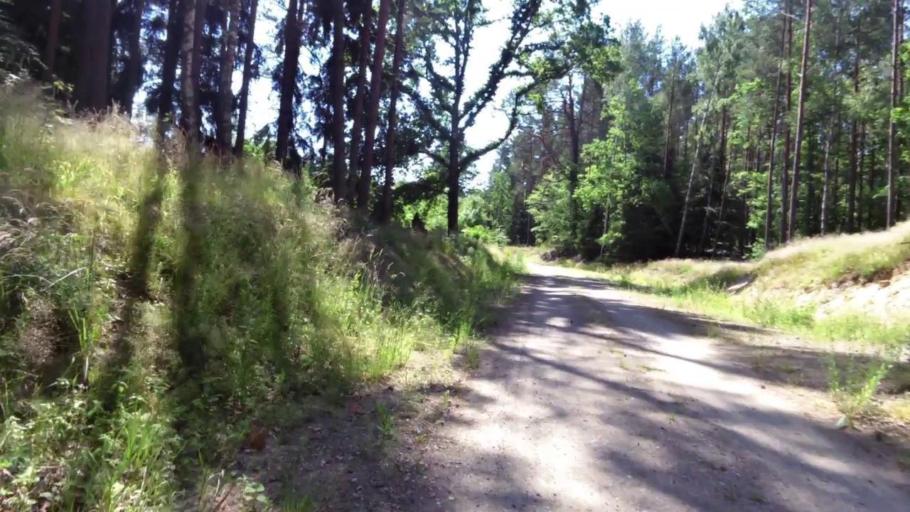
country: PL
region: West Pomeranian Voivodeship
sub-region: Powiat swidwinski
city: Polczyn-Zdroj
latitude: 53.7965
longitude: 16.1145
